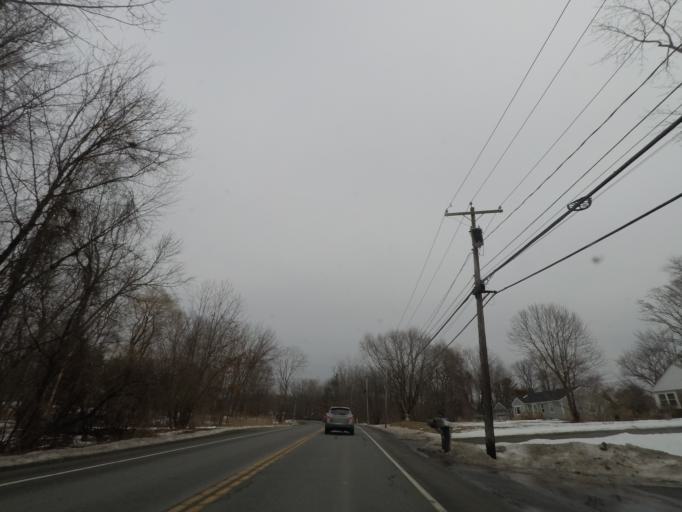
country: US
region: New York
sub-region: Albany County
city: Voorheesville
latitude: 42.7057
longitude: -73.9262
